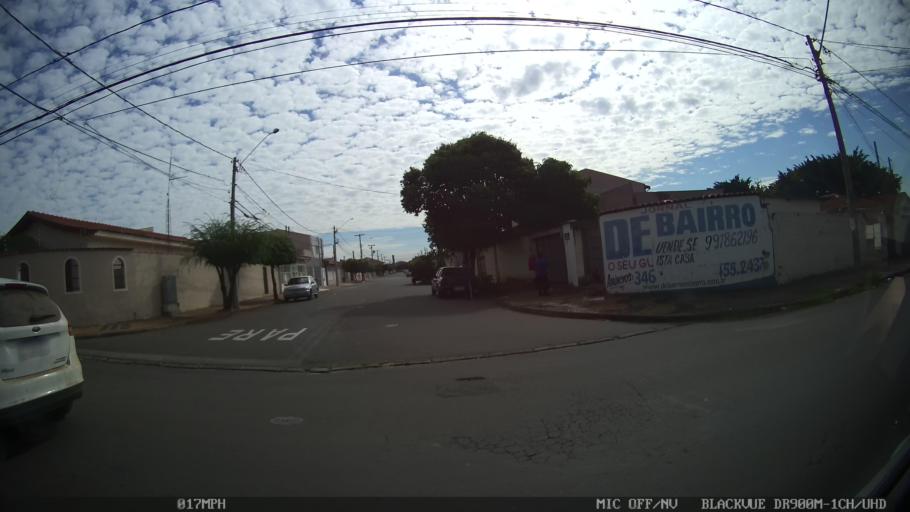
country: BR
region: Sao Paulo
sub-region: Santa Barbara D'Oeste
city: Santa Barbara d'Oeste
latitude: -22.7674
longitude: -47.3917
